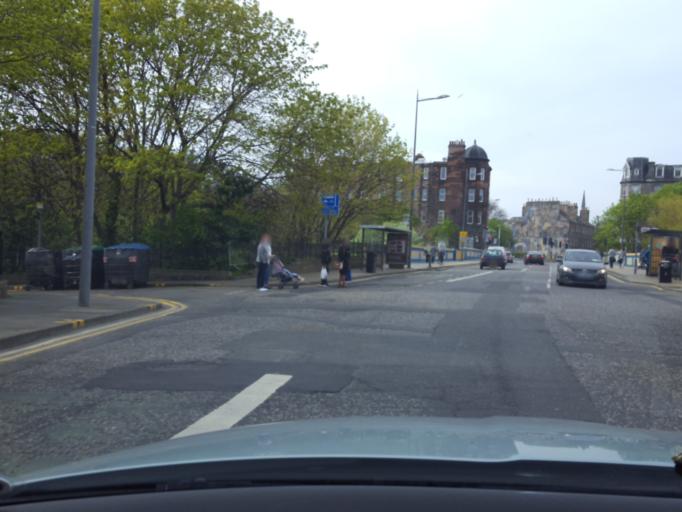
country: GB
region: Scotland
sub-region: Edinburgh
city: Edinburgh
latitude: 55.9745
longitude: -3.1781
